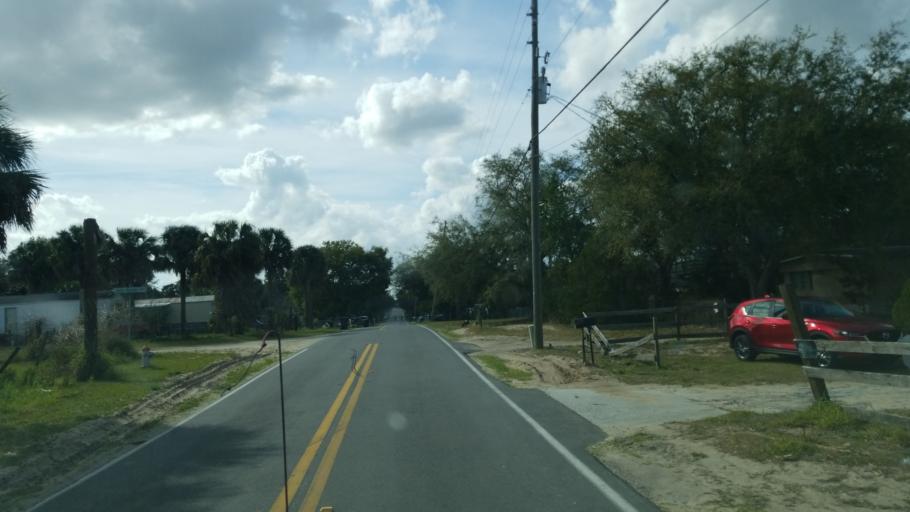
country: US
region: Florida
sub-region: Polk County
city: Davenport
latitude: 28.1466
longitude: -81.5846
